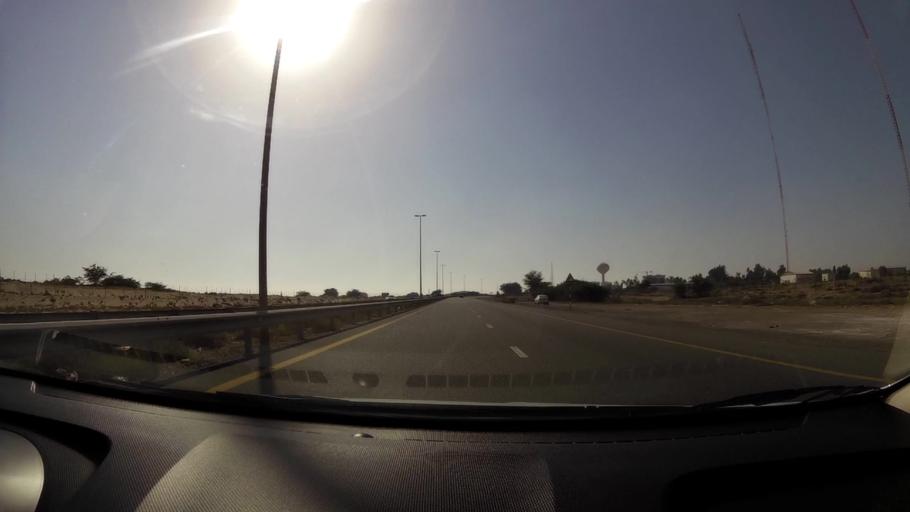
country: AE
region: Umm al Qaywayn
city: Umm al Qaywayn
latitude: 25.4848
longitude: 55.5567
